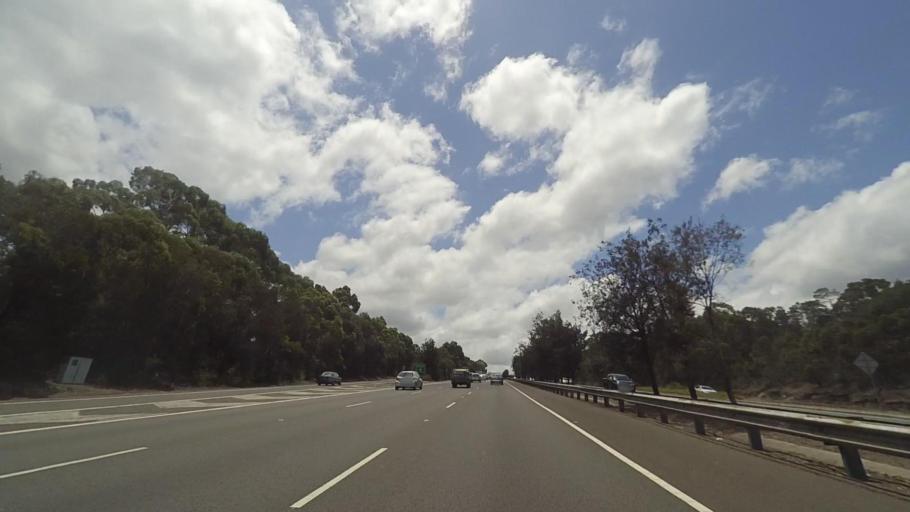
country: AU
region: New South Wales
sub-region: Hornsby Shire
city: Mount Colah
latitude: -33.6833
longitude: 151.1206
